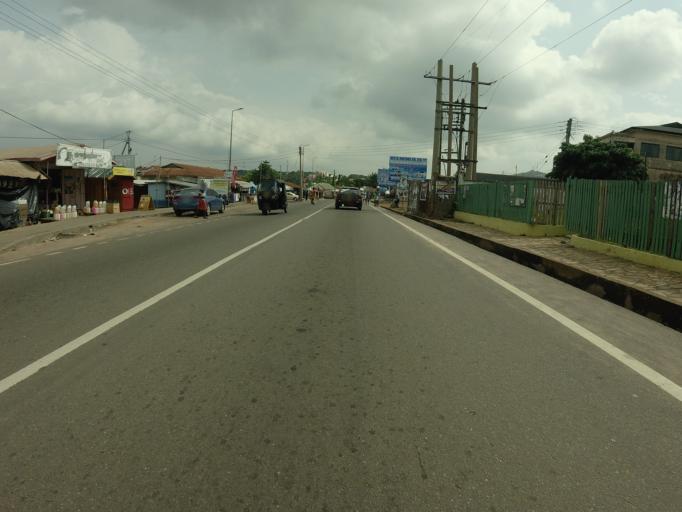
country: GH
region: Volta
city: Ho
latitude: 6.6174
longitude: 0.4679
